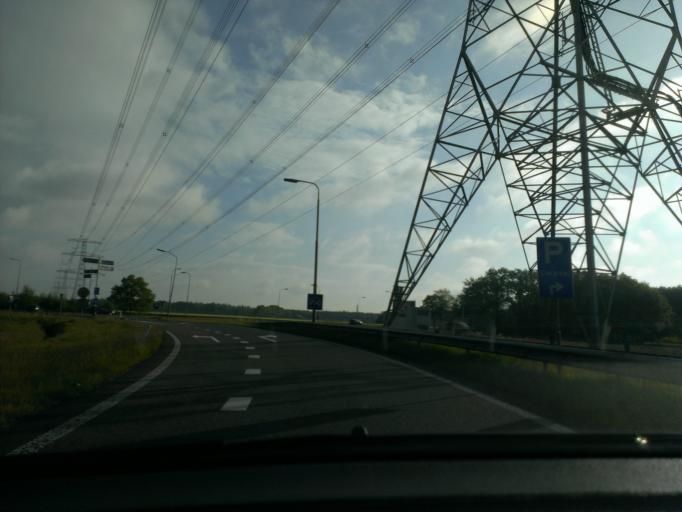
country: NL
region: Drenthe
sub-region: Gemeente Coevorden
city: Sleen
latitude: 52.7617
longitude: 6.8429
